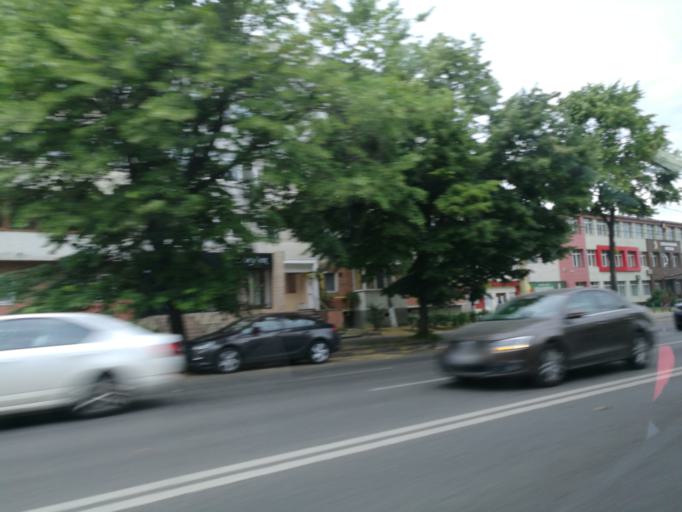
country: RO
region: Constanta
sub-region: Municipiul Constanta
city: Constanta
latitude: 44.1921
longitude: 28.6331
